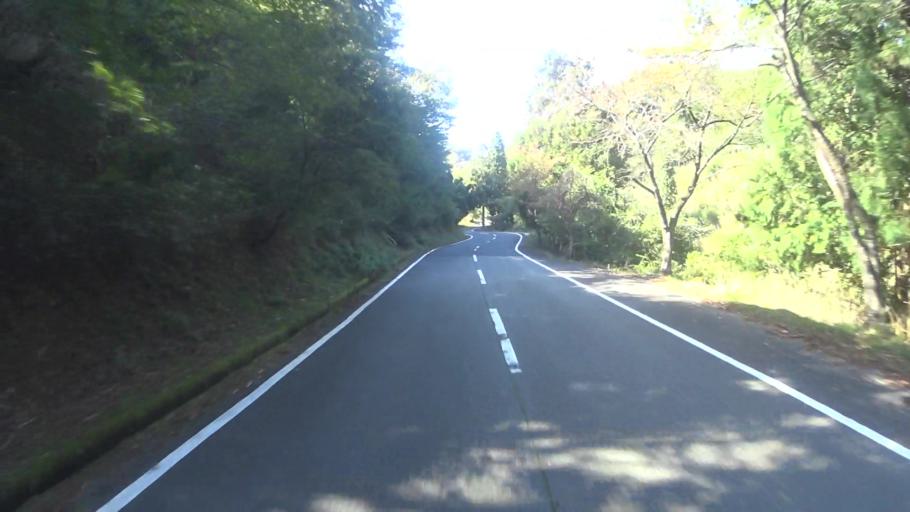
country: JP
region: Hyogo
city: Toyooka
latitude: 35.5350
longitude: 134.9250
